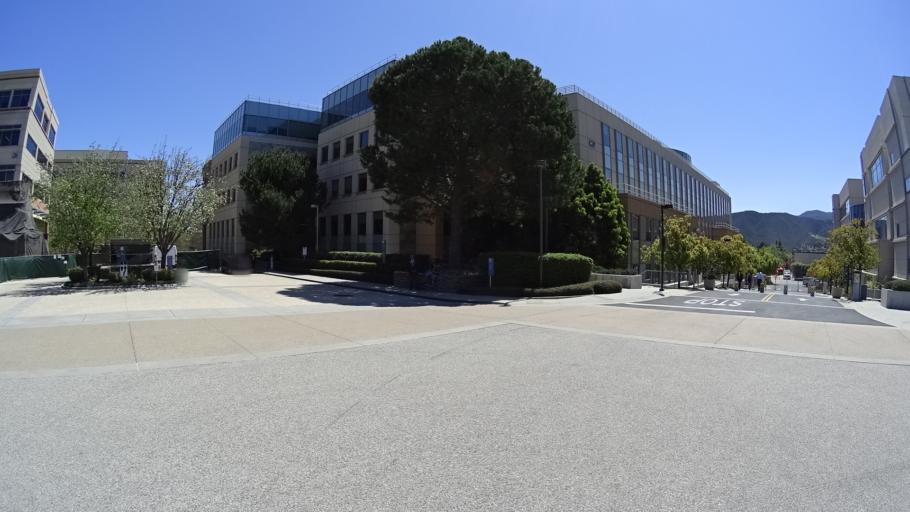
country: US
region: California
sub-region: Ventura County
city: Casa Conejo
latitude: 34.1911
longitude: -118.9211
